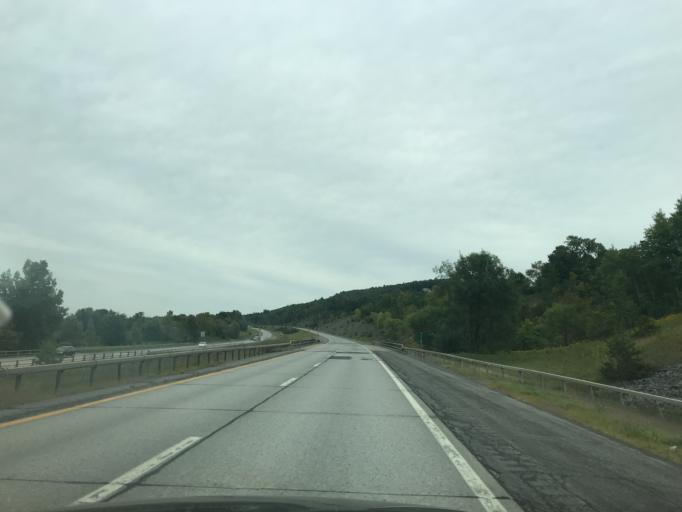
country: US
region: New York
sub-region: Schoharie County
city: Schoharie
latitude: 42.6811
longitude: -74.3726
